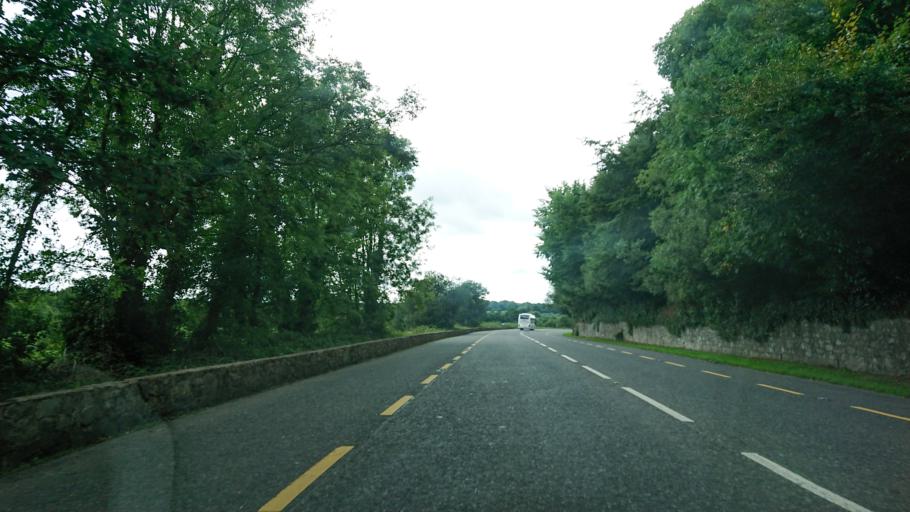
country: IE
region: Munster
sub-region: County Cork
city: Youghal
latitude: 52.1490
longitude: -7.8764
